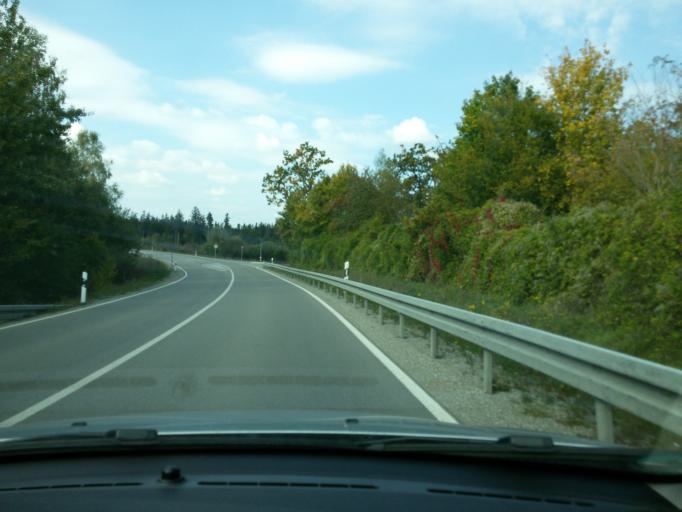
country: DE
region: Bavaria
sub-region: Upper Bavaria
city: Kaufering
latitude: 48.0804
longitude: 10.8467
